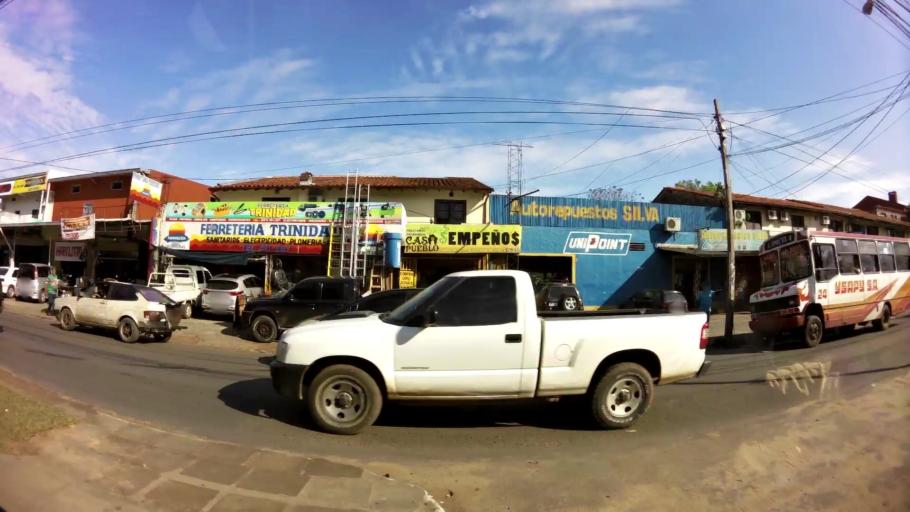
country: PY
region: Asuncion
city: Asuncion
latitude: -25.2576
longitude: -57.5857
